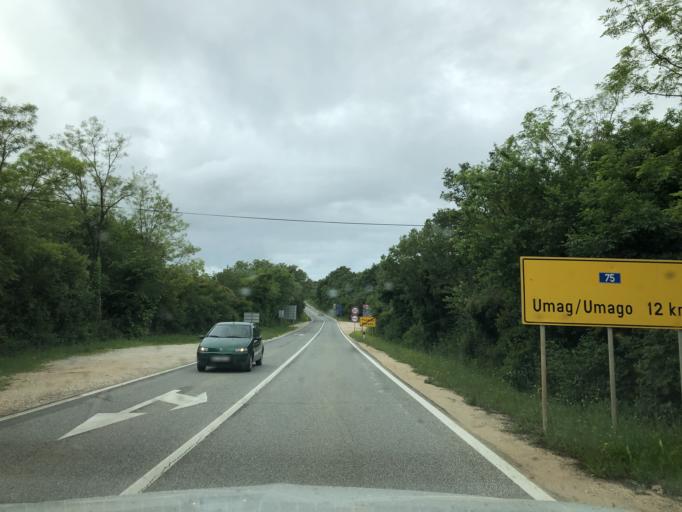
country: SI
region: Piran-Pirano
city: Seca
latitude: 45.4513
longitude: 13.6349
